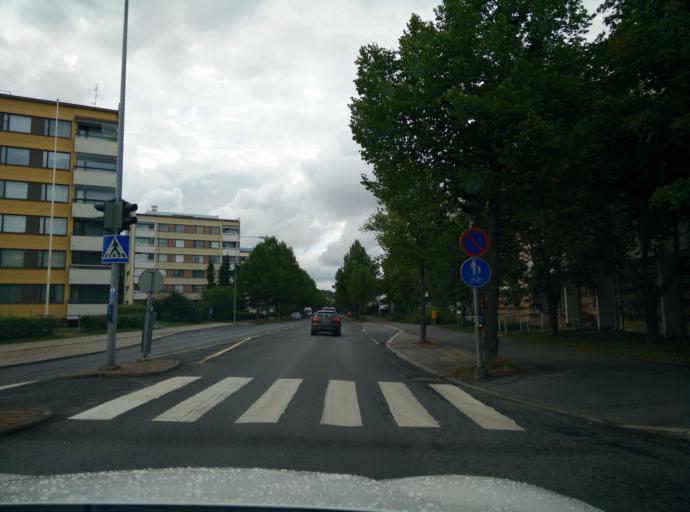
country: FI
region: Haeme
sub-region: Haemeenlinna
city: Haemeenlinna
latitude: 60.9968
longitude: 24.4415
